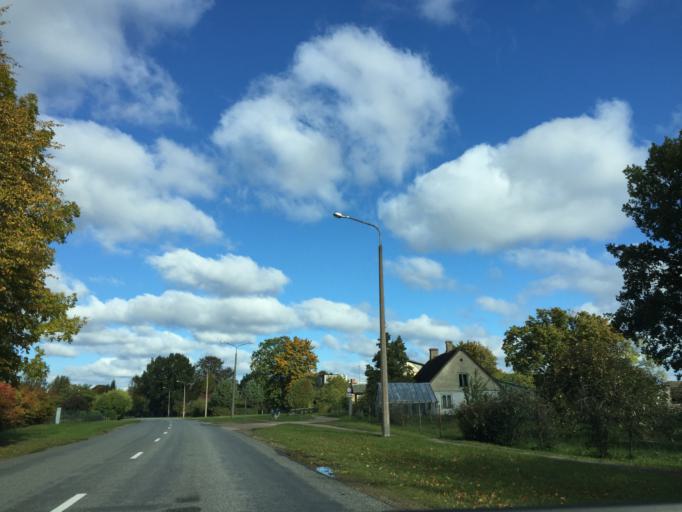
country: LV
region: Tukuma Rajons
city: Engure
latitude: 57.1509
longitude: 23.2308
